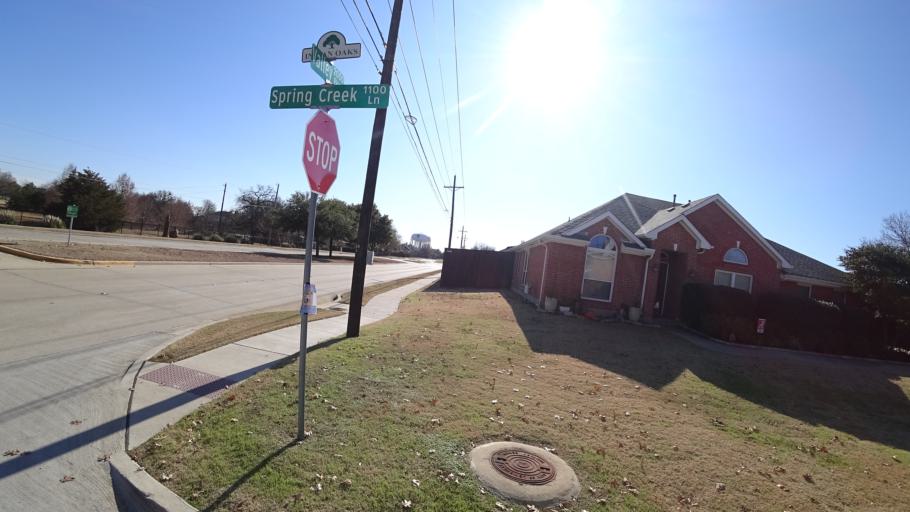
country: US
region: Texas
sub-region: Denton County
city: Lewisville
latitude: 33.0137
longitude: -97.0194
